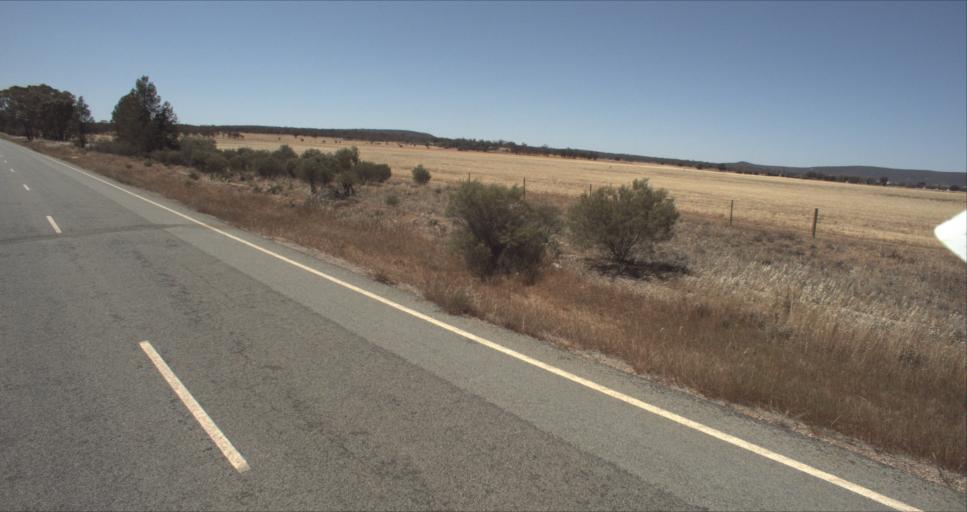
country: AU
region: New South Wales
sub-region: Leeton
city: Leeton
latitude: -34.4905
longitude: 146.4325
